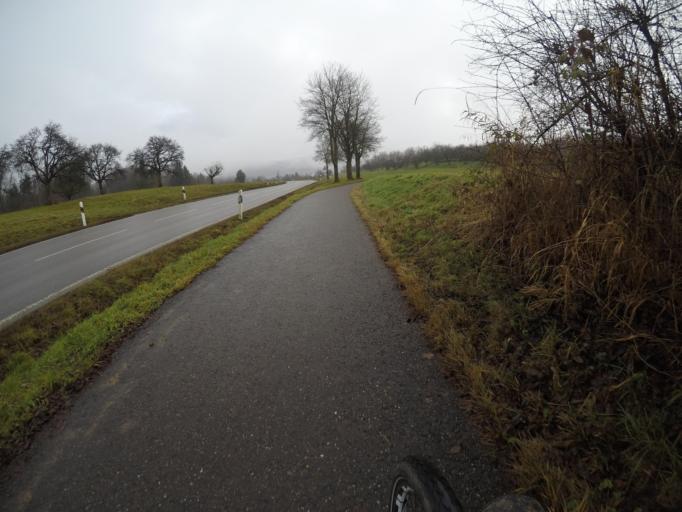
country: DE
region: Baden-Wuerttemberg
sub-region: Regierungsbezirk Stuttgart
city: Beuren
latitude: 48.5778
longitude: 9.3886
